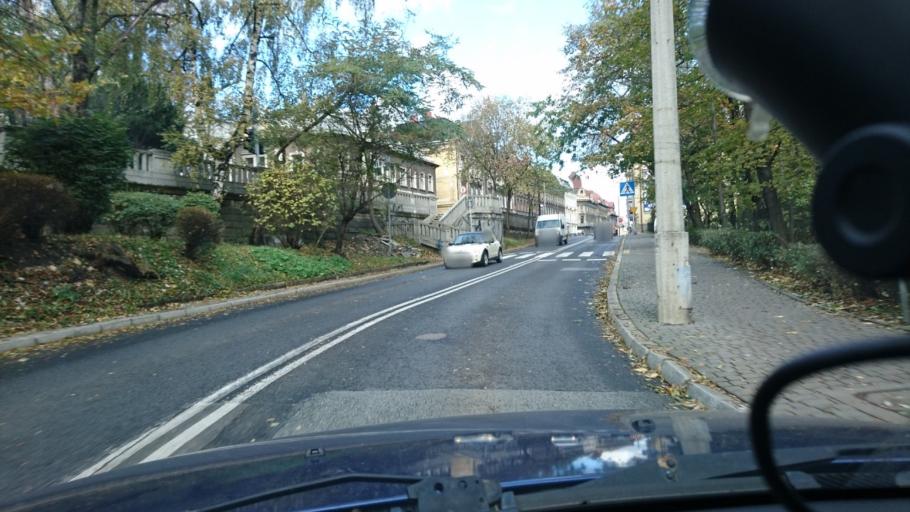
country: PL
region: Silesian Voivodeship
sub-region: Bielsko-Biala
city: Bielsko-Biala
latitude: 49.8257
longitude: 19.0453
